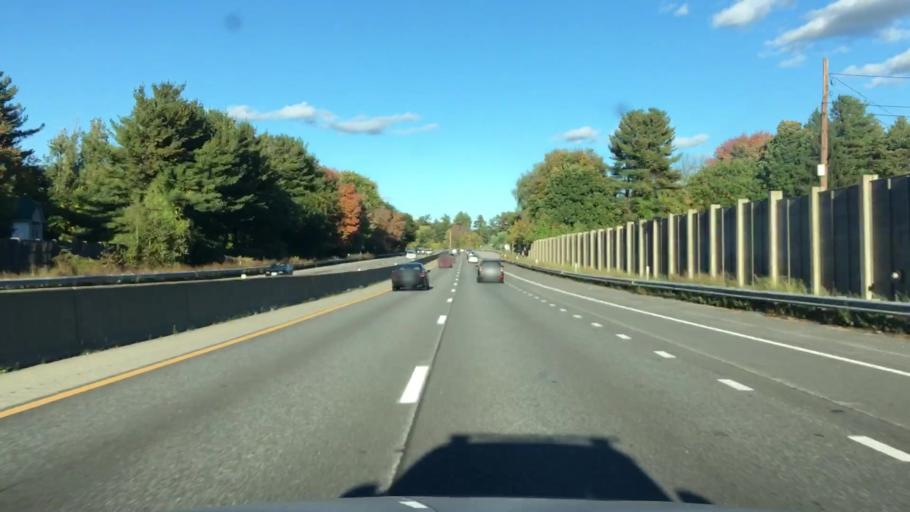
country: US
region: New Hampshire
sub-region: Rockingham County
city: Auburn
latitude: 43.0086
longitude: -71.3894
